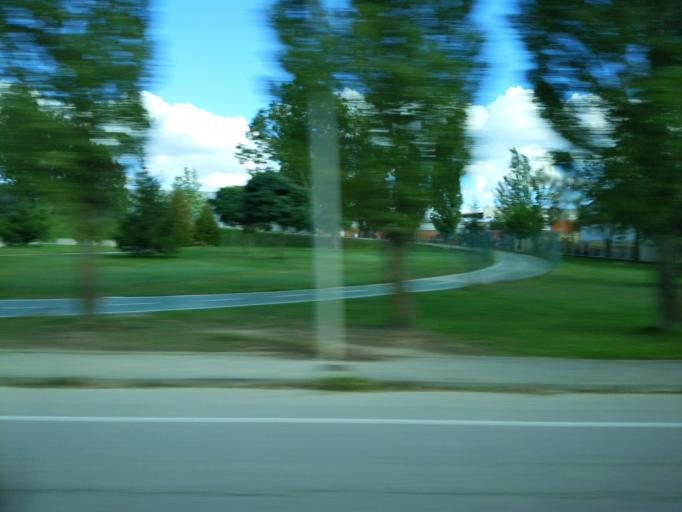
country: ES
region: Castille and Leon
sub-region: Provincia de Soria
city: Soria
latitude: 41.7785
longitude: -2.4904
